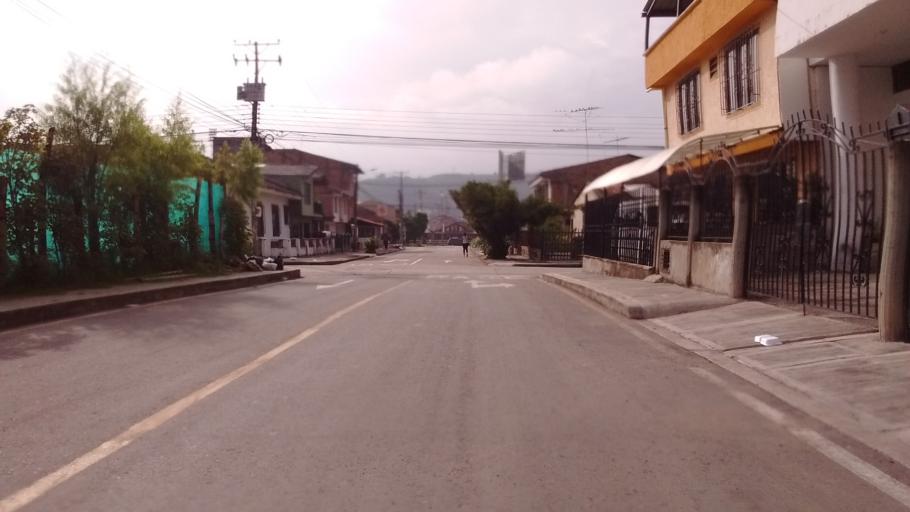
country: CO
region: Cauca
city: Popayan
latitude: 2.4555
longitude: -76.5941
